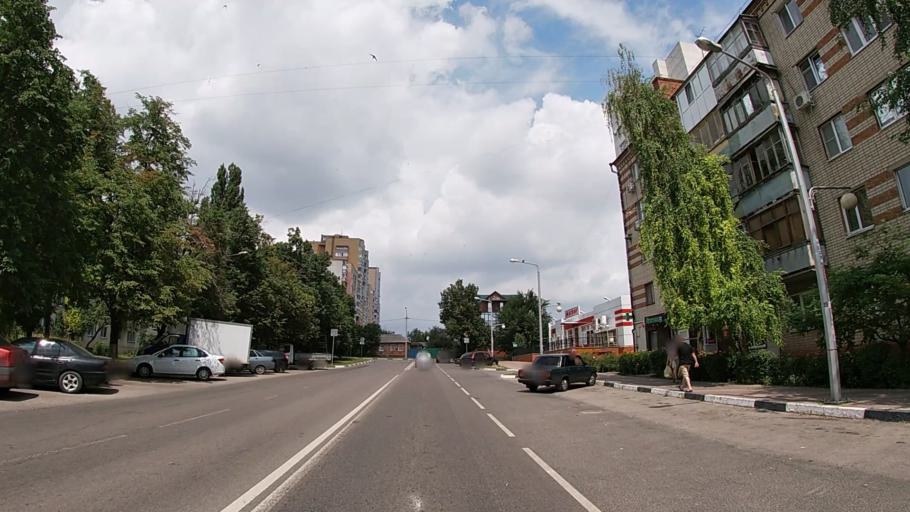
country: RU
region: Belgorod
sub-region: Belgorodskiy Rayon
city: Belgorod
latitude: 50.6053
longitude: 36.5959
